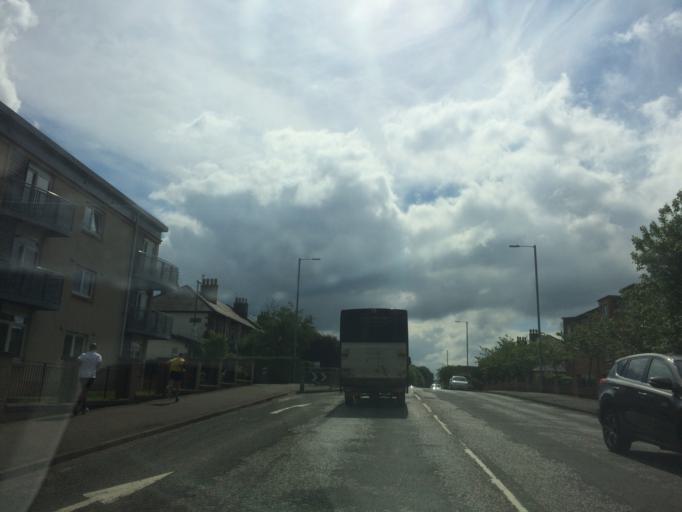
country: GB
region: Scotland
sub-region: East Renfrewshire
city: Giffnock
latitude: 55.8190
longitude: -4.2963
